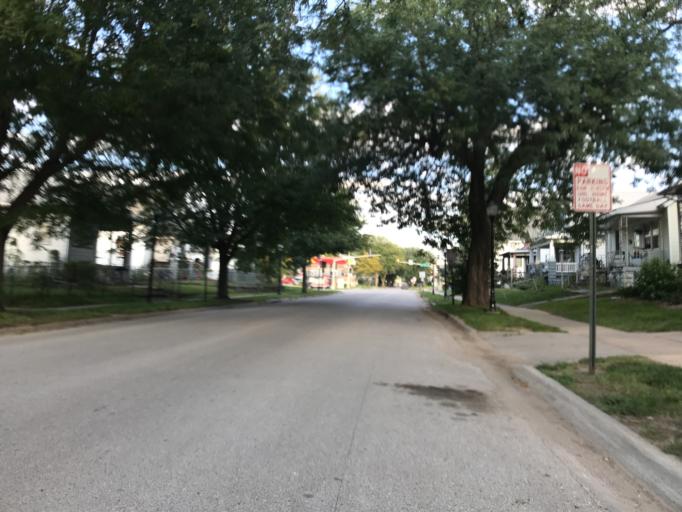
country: US
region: Nebraska
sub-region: Lancaster County
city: Lincoln
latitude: 40.8256
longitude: -96.7082
